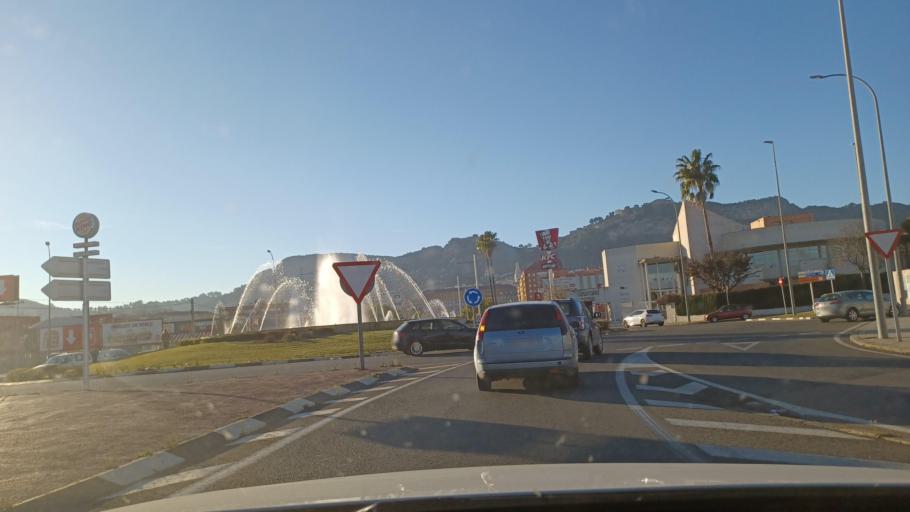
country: ES
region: Valencia
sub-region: Provincia de Valencia
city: Xativa
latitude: 38.9965
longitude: -0.5213
